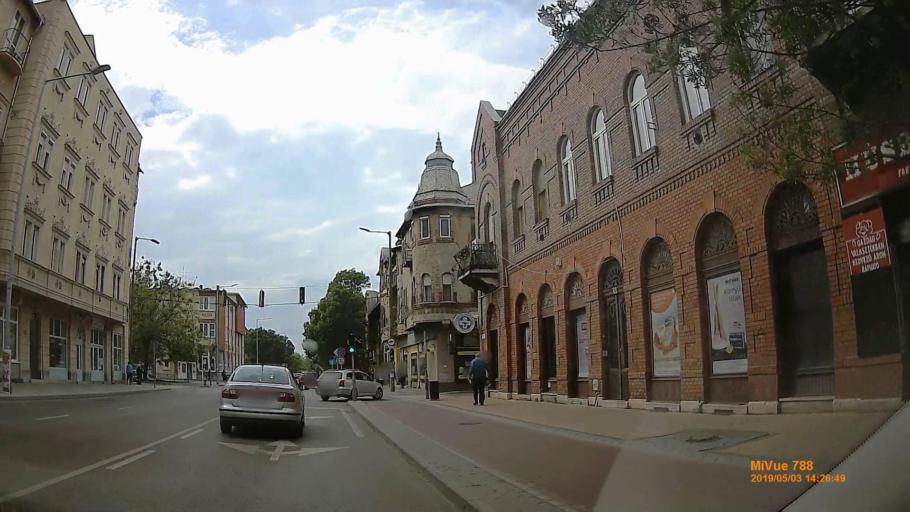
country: HU
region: Jasz-Nagykun-Szolnok
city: Szolnok
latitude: 47.1761
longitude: 20.1896
